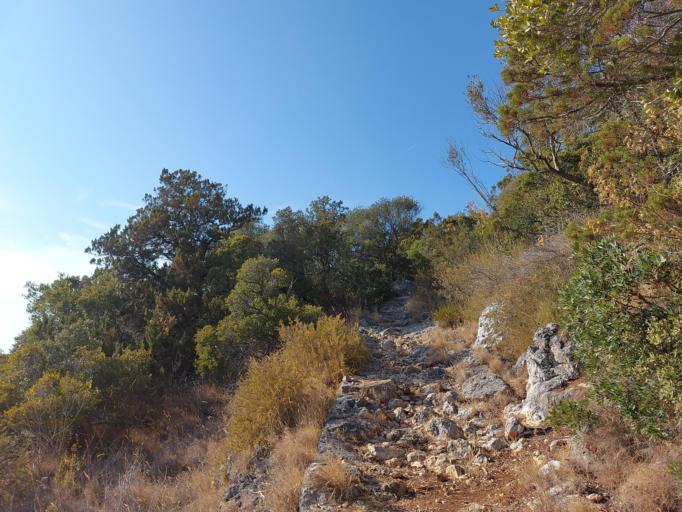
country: HR
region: Dubrovacko-Neretvanska
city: Smokvica
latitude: 42.7663
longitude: 16.8055
